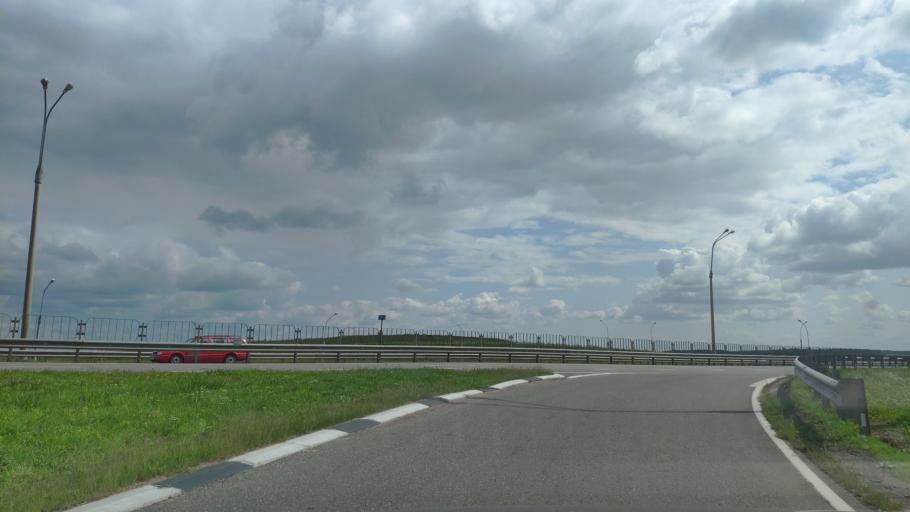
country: BY
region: Minsk
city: Zaslawye
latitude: 54.0071
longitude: 27.3090
